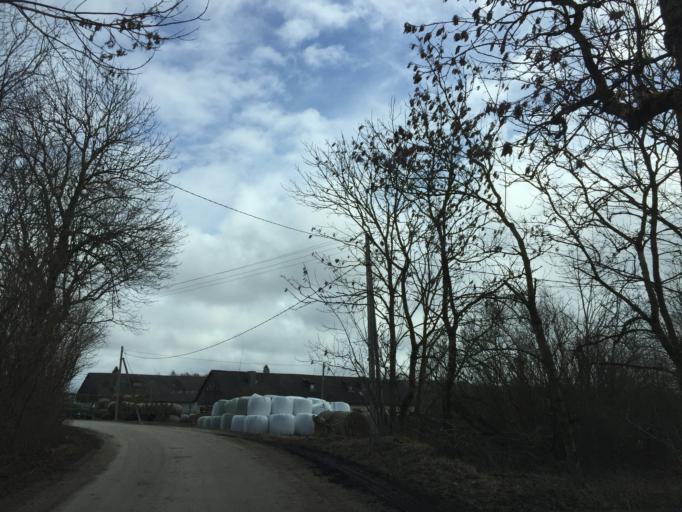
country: EE
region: Laeaene
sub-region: Lihula vald
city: Lihula
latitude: 58.7333
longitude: 23.8634
